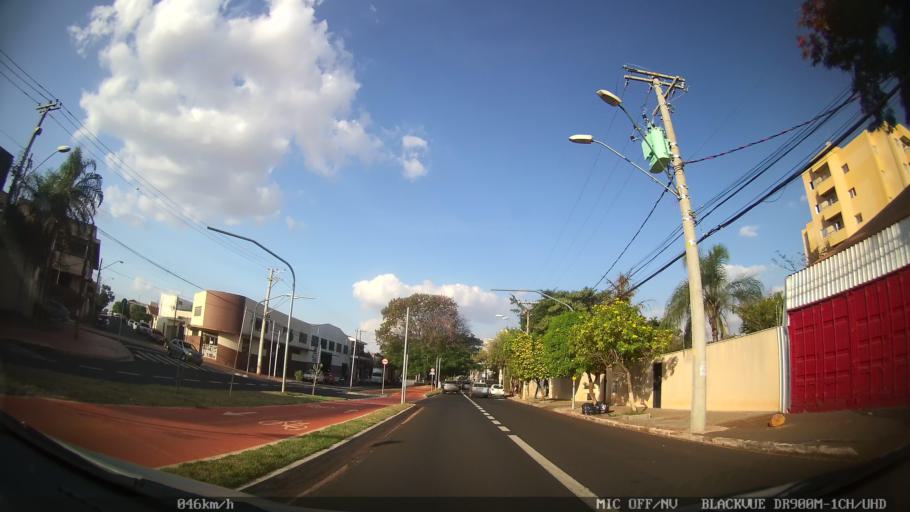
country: BR
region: Sao Paulo
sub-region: Ribeirao Preto
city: Ribeirao Preto
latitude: -21.1748
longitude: -47.8358
